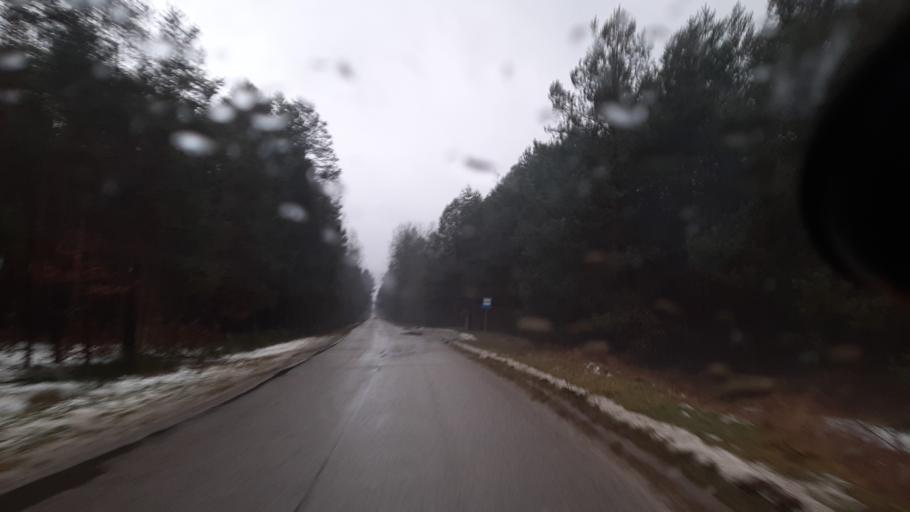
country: PL
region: Lublin Voivodeship
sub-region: Powiat lubartowski
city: Kamionka
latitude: 51.5105
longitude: 22.4907
